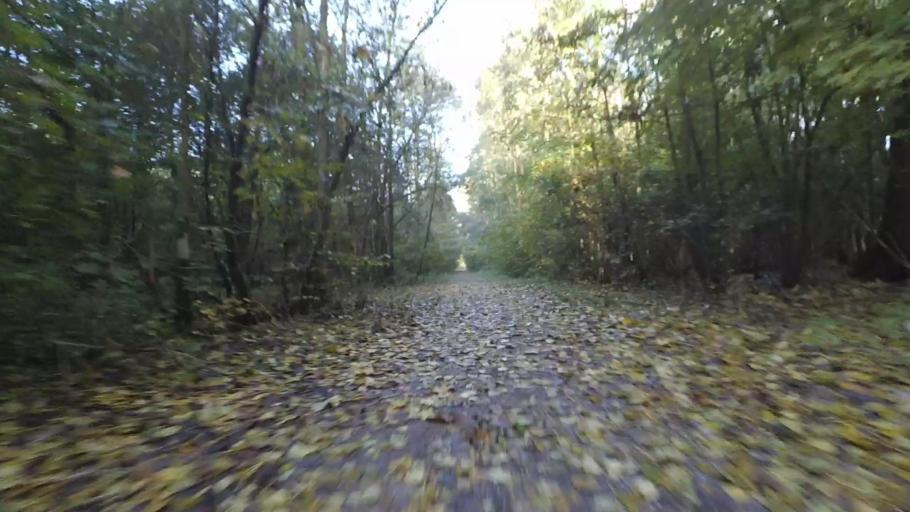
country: NL
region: Flevoland
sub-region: Gemeente Zeewolde
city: Zeewolde
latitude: 52.3014
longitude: 5.5304
